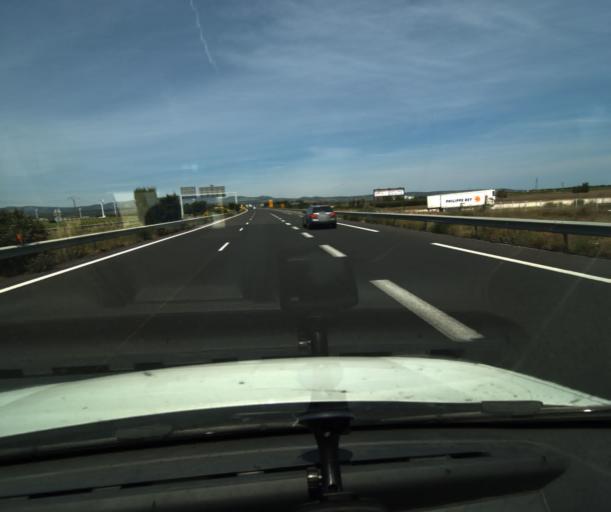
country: FR
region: Languedoc-Roussillon
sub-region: Departement des Pyrenees-Orientales
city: Rivesaltes
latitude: 42.7868
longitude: 2.8956
